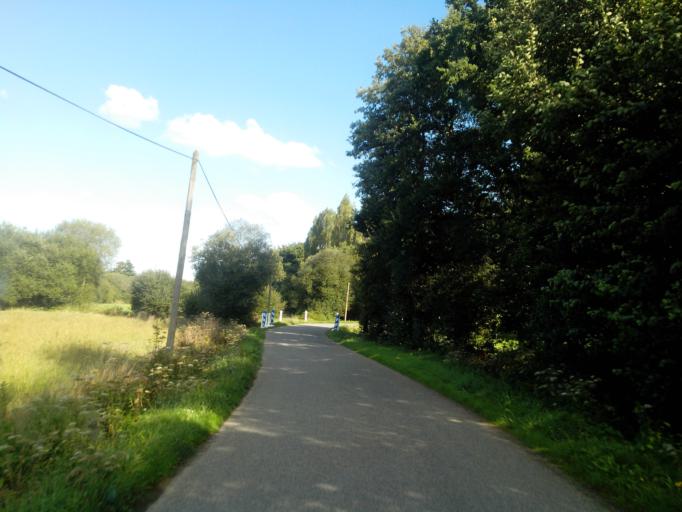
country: FR
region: Brittany
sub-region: Departement des Cotes-d'Armor
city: Merdrignac
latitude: 48.1546
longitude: -2.4157
